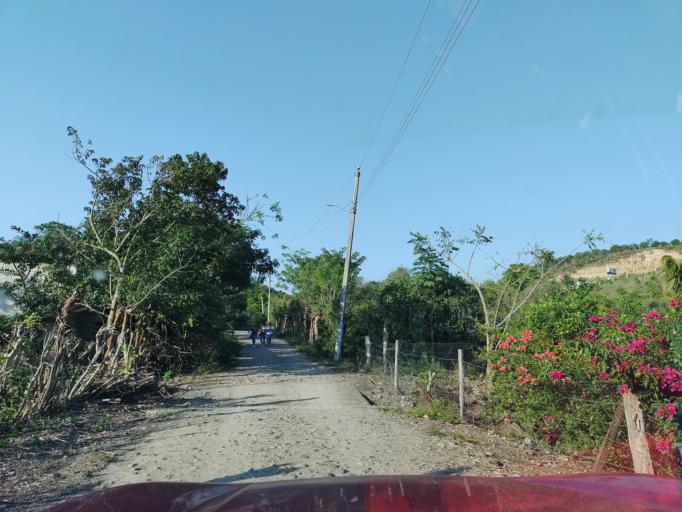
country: MX
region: Veracruz
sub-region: Papantla
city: Polutla
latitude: 20.4490
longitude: -97.2428
